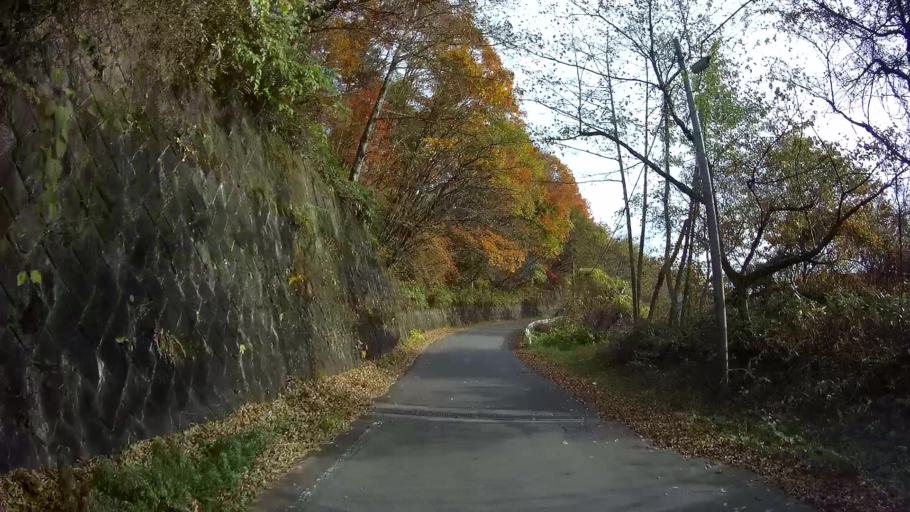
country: JP
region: Gunma
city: Nakanojomachi
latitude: 36.6410
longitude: 138.6425
